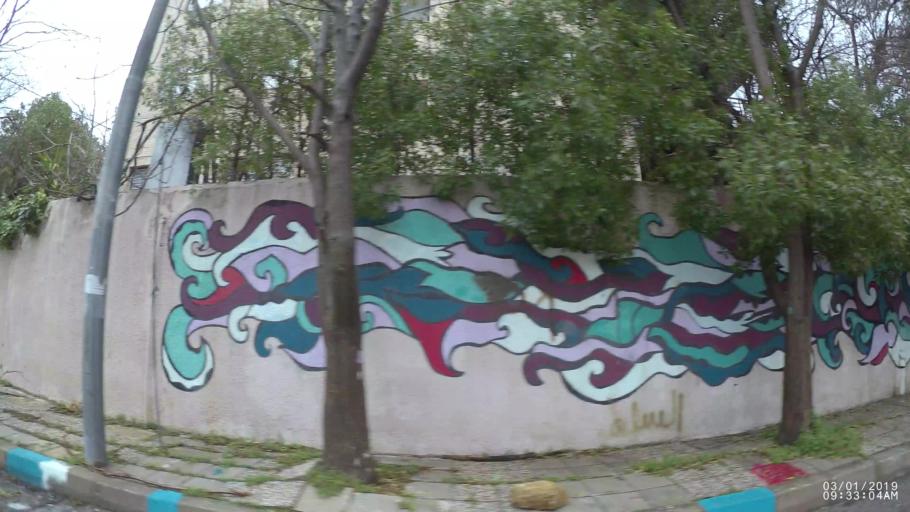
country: JO
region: Amman
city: Wadi as Sir
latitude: 31.9693
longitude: 35.8451
